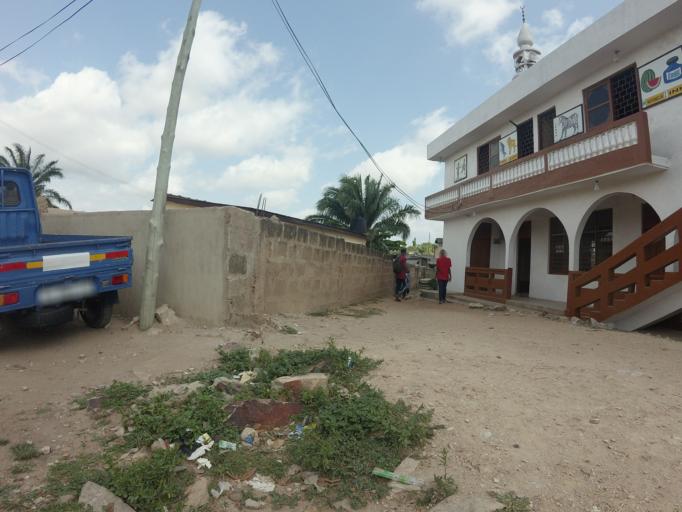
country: GH
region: Greater Accra
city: Dome
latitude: 5.6150
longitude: -0.2431
